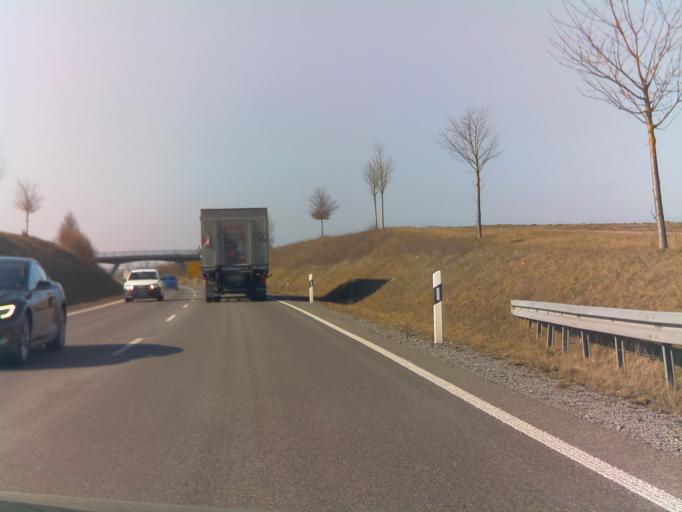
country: DE
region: Baden-Wuerttemberg
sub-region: Regierungsbezirk Stuttgart
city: Motzingen
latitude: 48.5046
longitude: 8.7984
